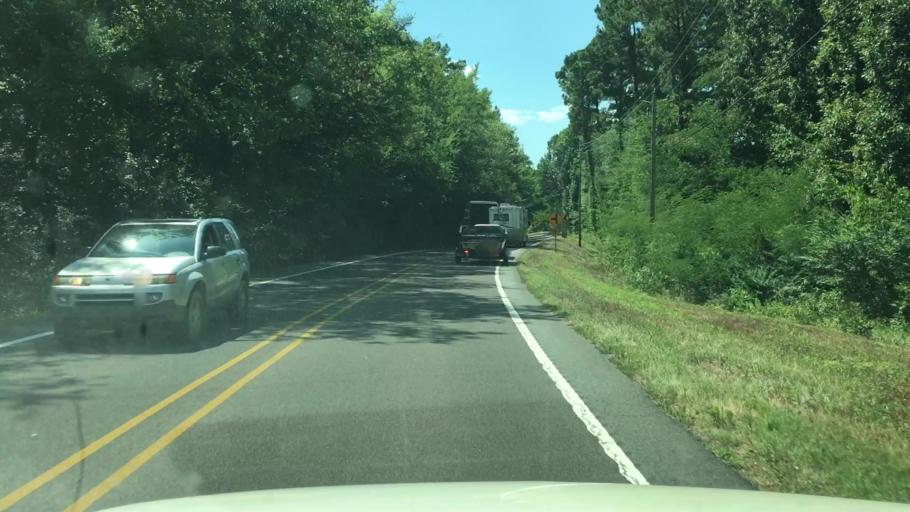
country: US
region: Arkansas
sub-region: Garland County
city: Piney
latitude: 34.5096
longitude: -93.1672
